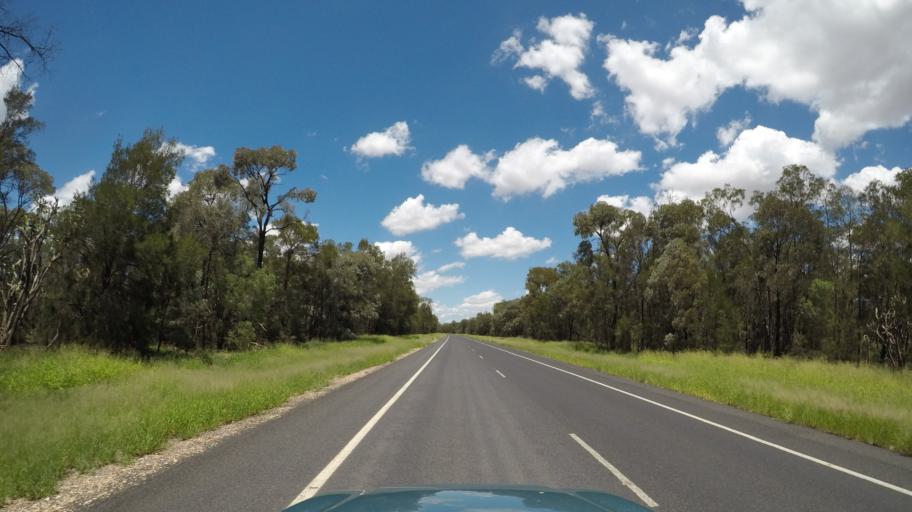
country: AU
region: Queensland
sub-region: Goondiwindi
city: Goondiwindi
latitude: -28.0864
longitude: 150.7337
